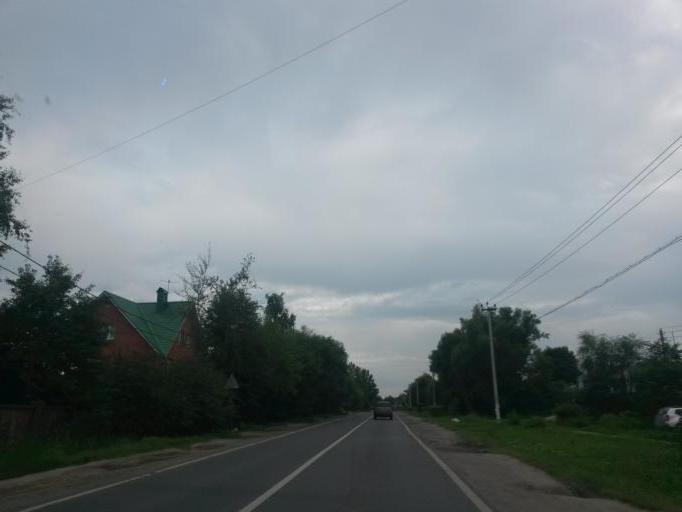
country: RU
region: Moskovskaya
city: Vostryakovo
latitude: 55.4031
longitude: 37.8175
